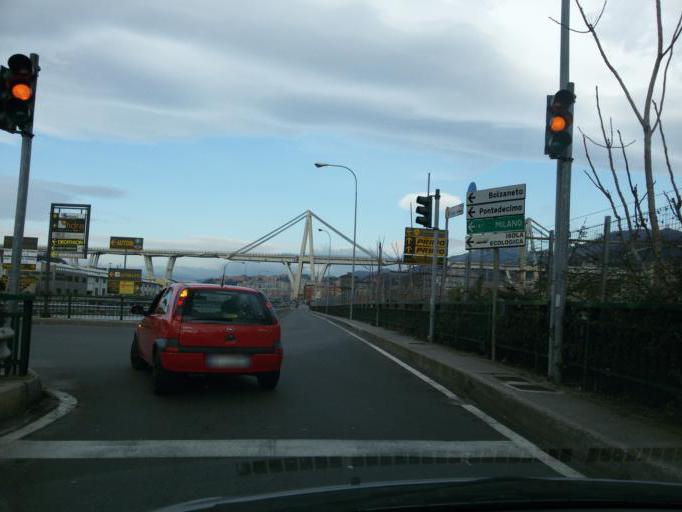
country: IT
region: Liguria
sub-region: Provincia di Genova
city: San Teodoro
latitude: 44.4216
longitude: 8.8856
